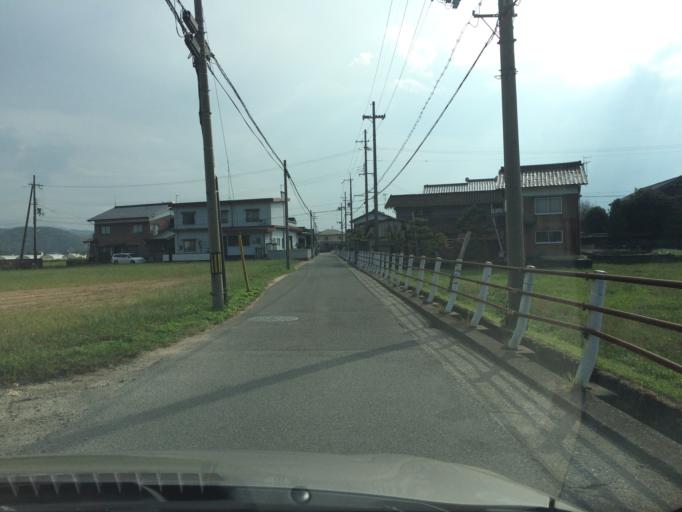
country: JP
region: Hyogo
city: Toyooka
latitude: 35.5227
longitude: 134.8275
